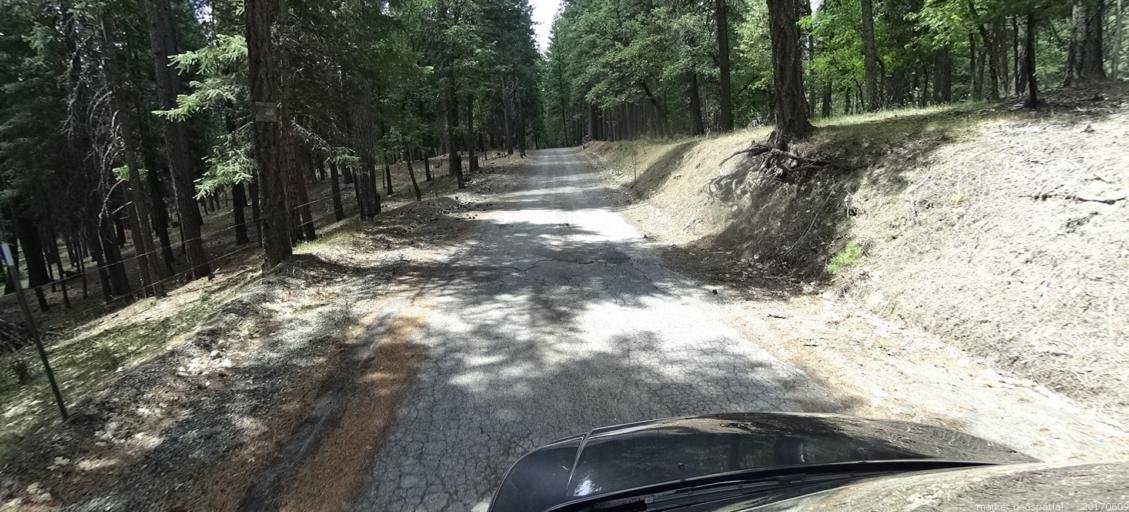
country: US
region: California
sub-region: Siskiyou County
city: Yreka
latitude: 41.3524
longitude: -122.9036
